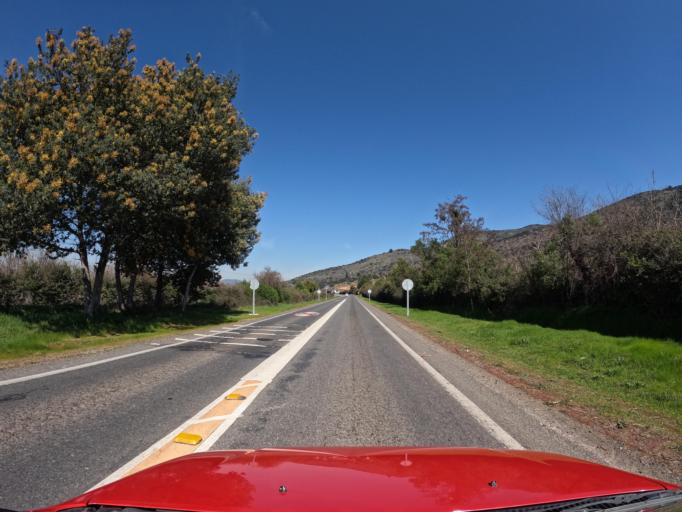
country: CL
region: Maule
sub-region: Provincia de Curico
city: Rauco
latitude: -35.0628
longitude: -71.6202
